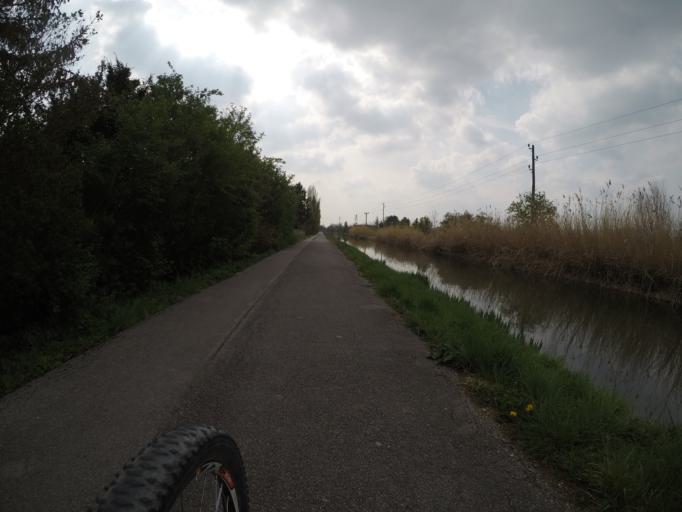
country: AT
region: Lower Austria
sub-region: Politischer Bezirk Baden
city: Pfaffstatten
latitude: 48.0049
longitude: 16.2622
